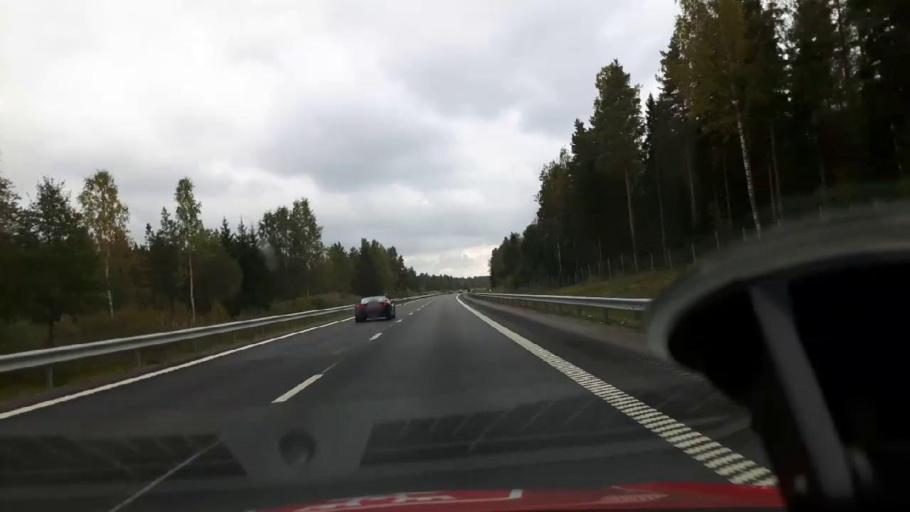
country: SE
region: Gaevleborg
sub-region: Gavle Kommun
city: Gavle
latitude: 60.6078
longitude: 17.1767
